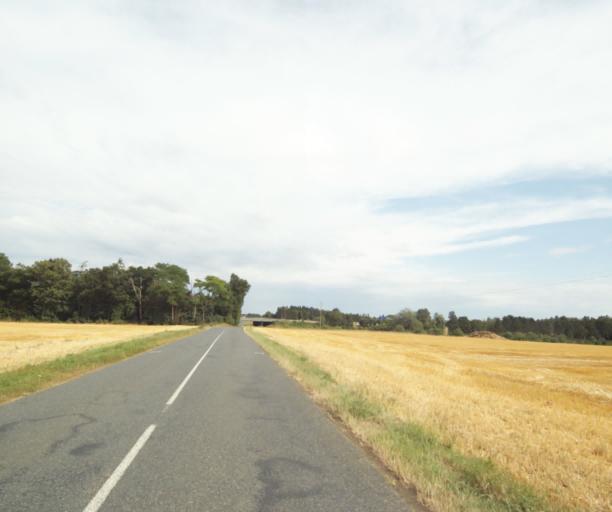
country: FR
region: Ile-de-France
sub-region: Departement de Seine-et-Marne
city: Acheres-la-Foret
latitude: 48.3474
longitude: 2.5858
